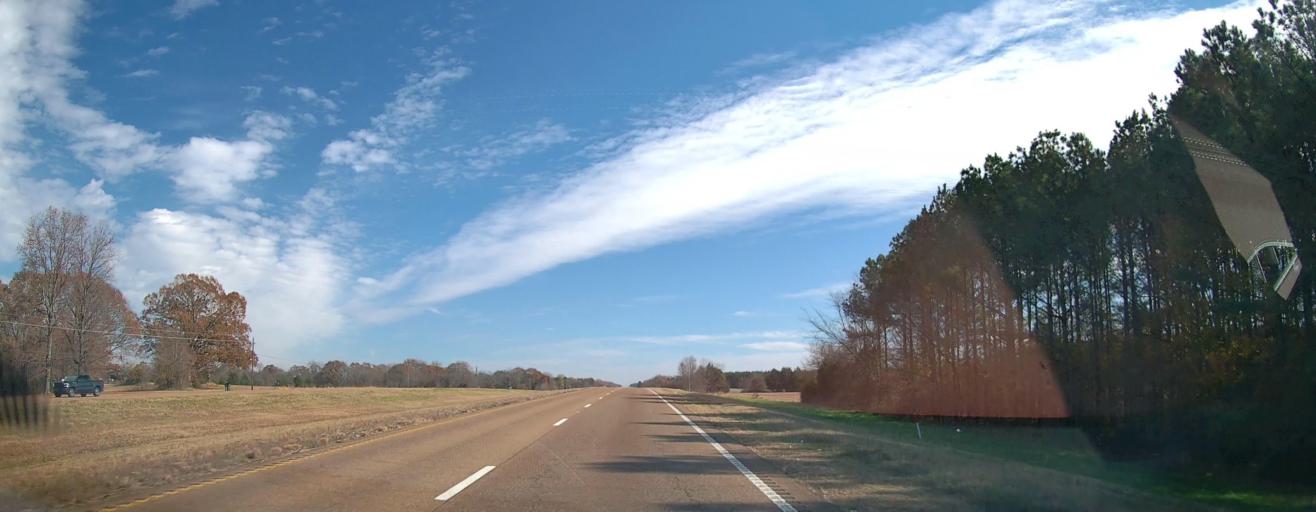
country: US
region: Mississippi
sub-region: Marshall County
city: Holly Springs
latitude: 34.9461
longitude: -89.3689
